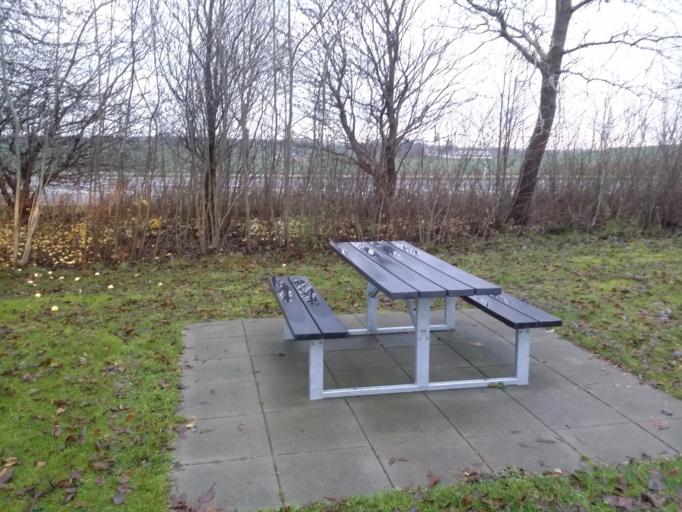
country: DK
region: Capital Region
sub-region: Frederikssund Kommune
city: Slangerup
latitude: 55.8316
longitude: 12.1644
